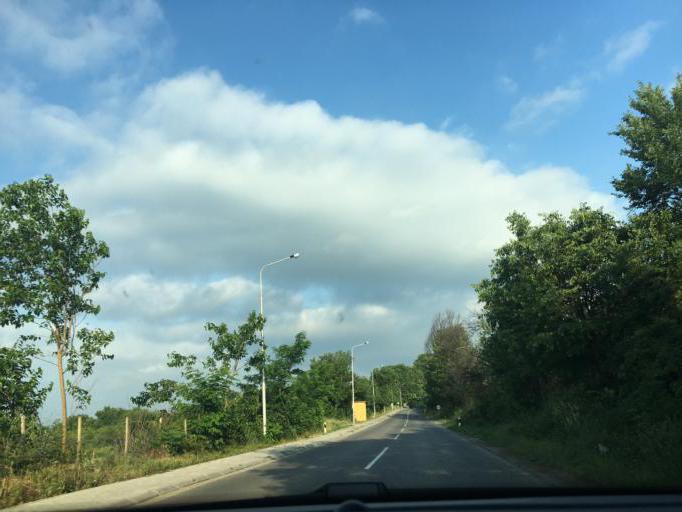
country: MK
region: Valandovo
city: Valandovo
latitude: 41.3193
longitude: 22.5740
